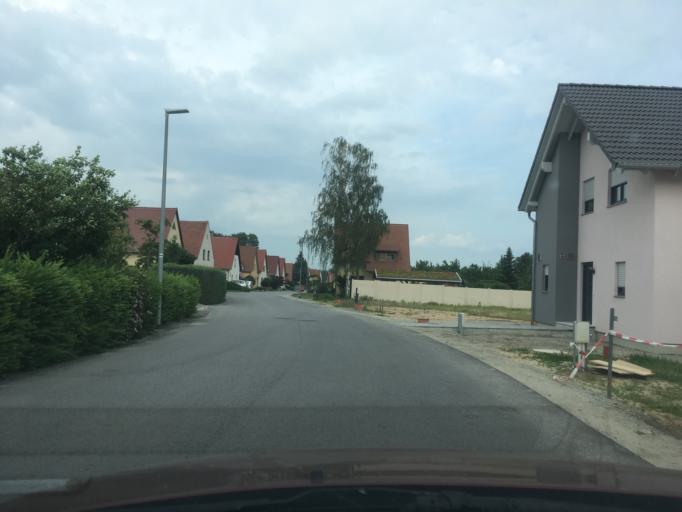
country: DE
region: Saxony
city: Bautzen
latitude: 51.1704
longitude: 14.4485
